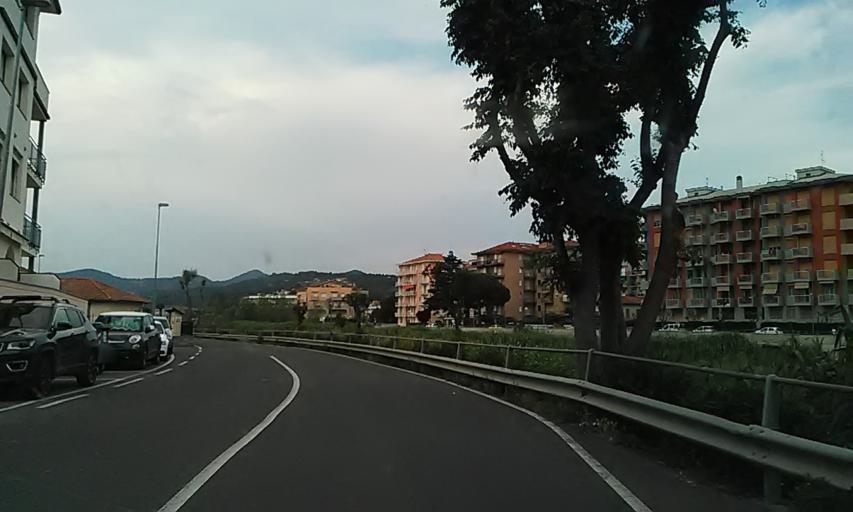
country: IT
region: Liguria
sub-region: Provincia di Savona
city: Andora
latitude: 43.9512
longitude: 8.1426
